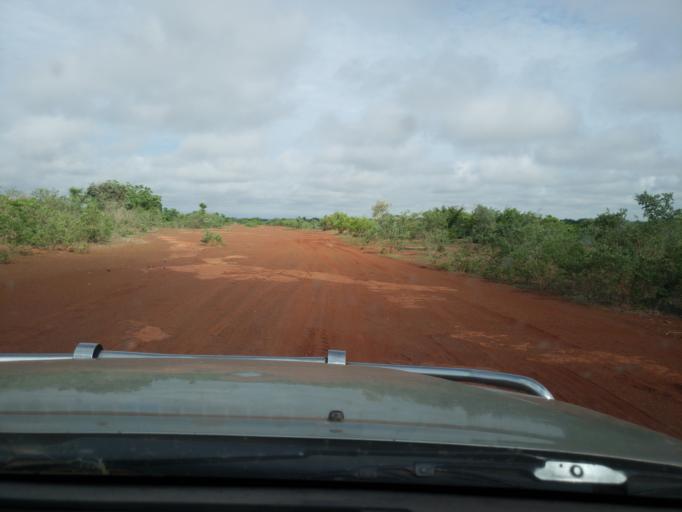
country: ML
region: Sikasso
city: Koutiala
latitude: 12.3925
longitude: -5.9925
